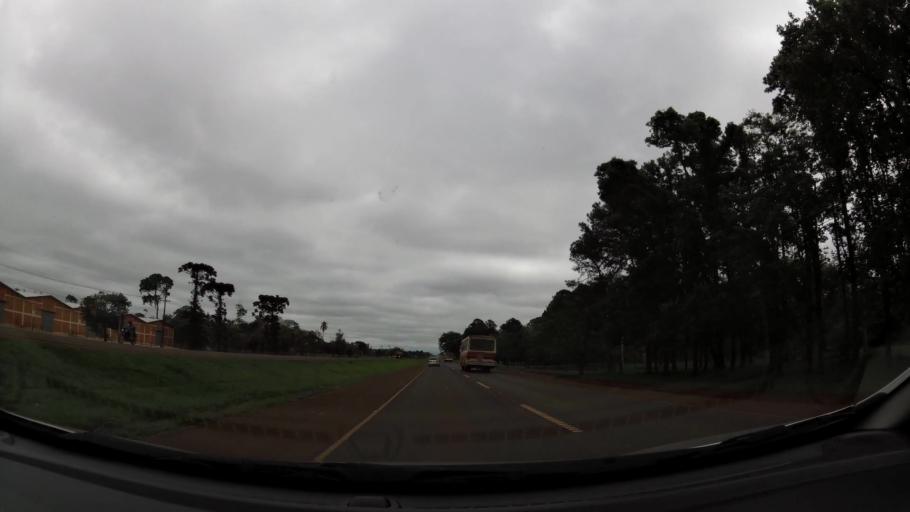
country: PY
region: Alto Parana
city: Colonia Yguazu
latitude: -25.4881
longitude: -54.8176
